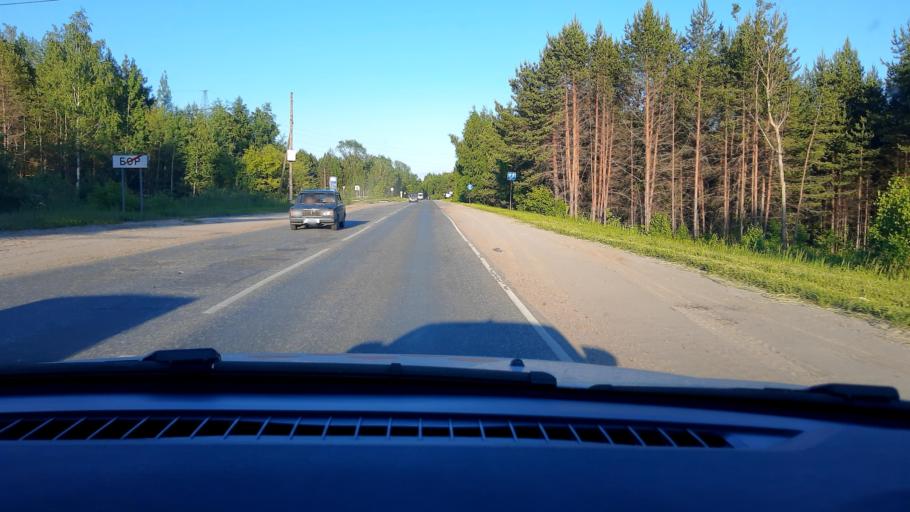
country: RU
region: Nizjnij Novgorod
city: Bor
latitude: 56.3256
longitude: 44.1376
